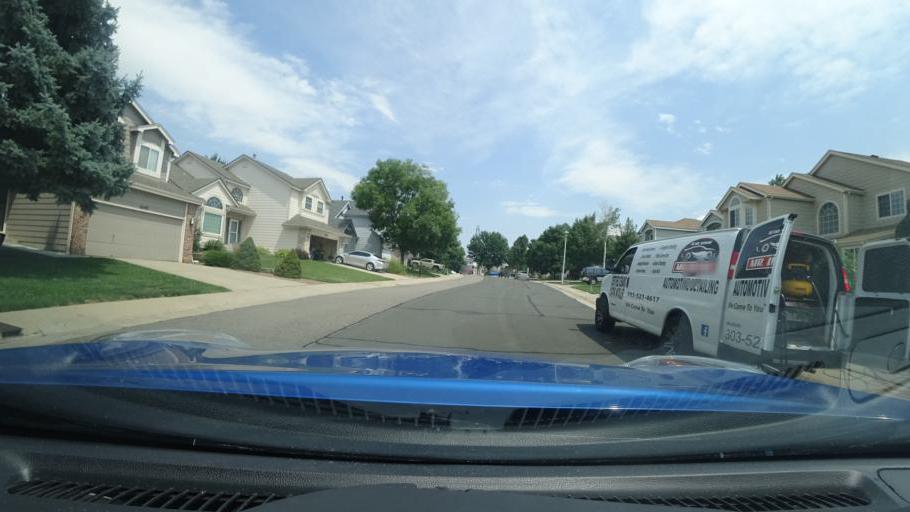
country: US
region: Colorado
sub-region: Adams County
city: Aurora
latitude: 39.6703
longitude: -104.7748
